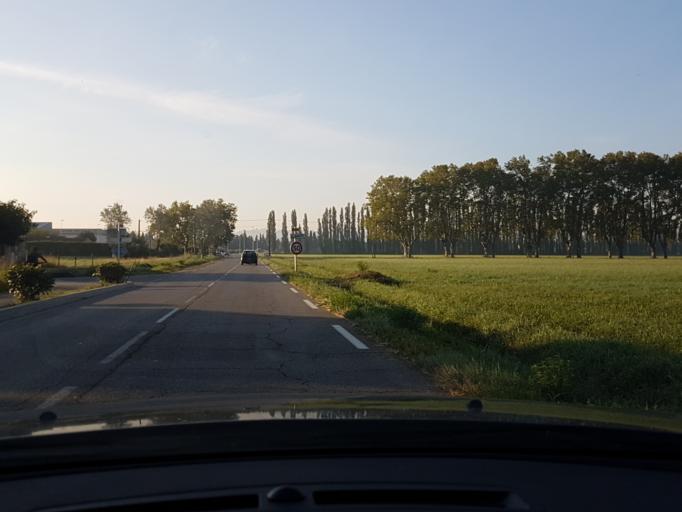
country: FR
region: Provence-Alpes-Cote d'Azur
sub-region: Departement des Bouches-du-Rhone
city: Saint-Andiol
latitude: 43.8241
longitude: 4.9464
